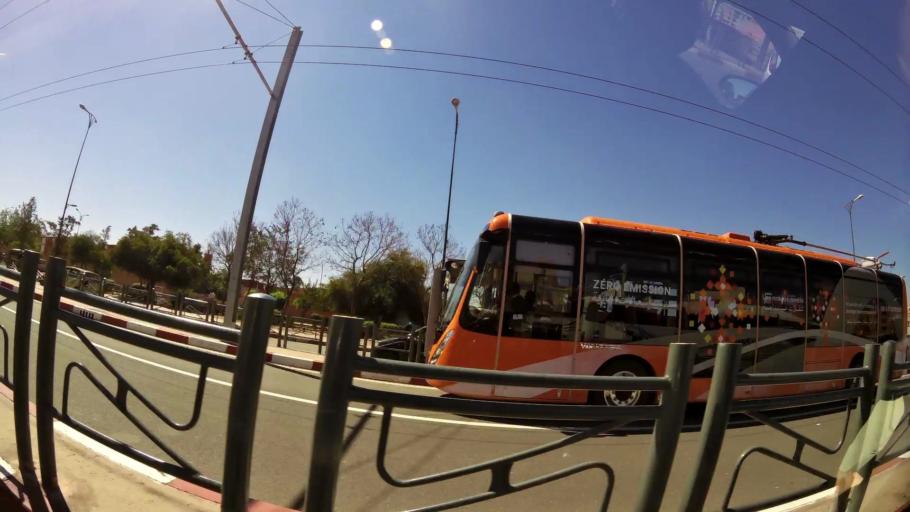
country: MA
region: Marrakech-Tensift-Al Haouz
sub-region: Marrakech
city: Marrakesh
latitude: 31.6278
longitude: -8.0580
